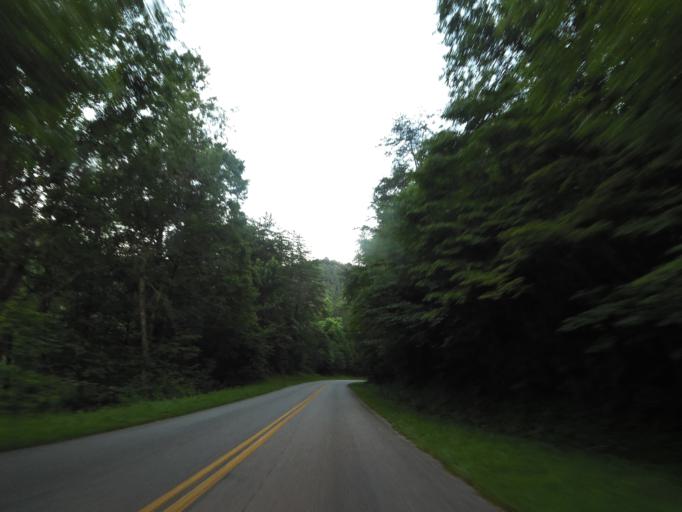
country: US
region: Tennessee
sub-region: Blount County
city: Maryville
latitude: 35.5691
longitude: -84.0026
